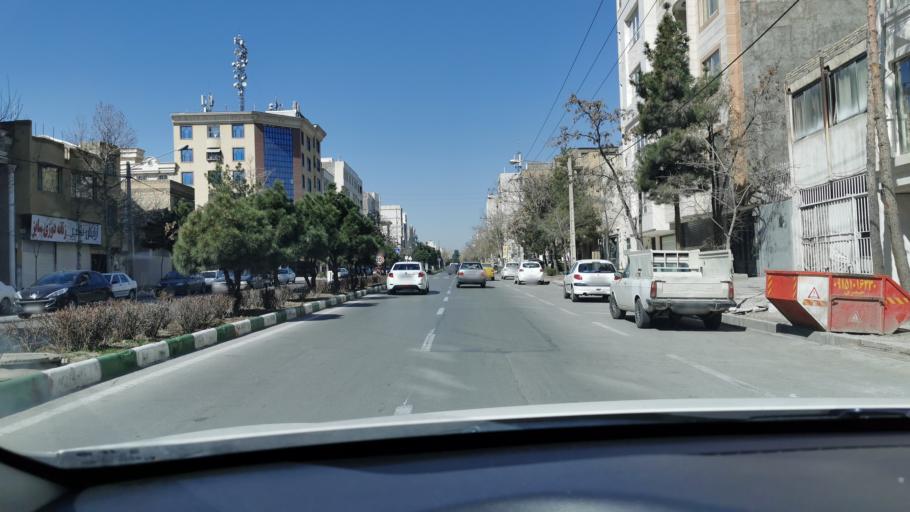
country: IR
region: Razavi Khorasan
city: Mashhad
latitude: 36.3252
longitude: 59.5242
